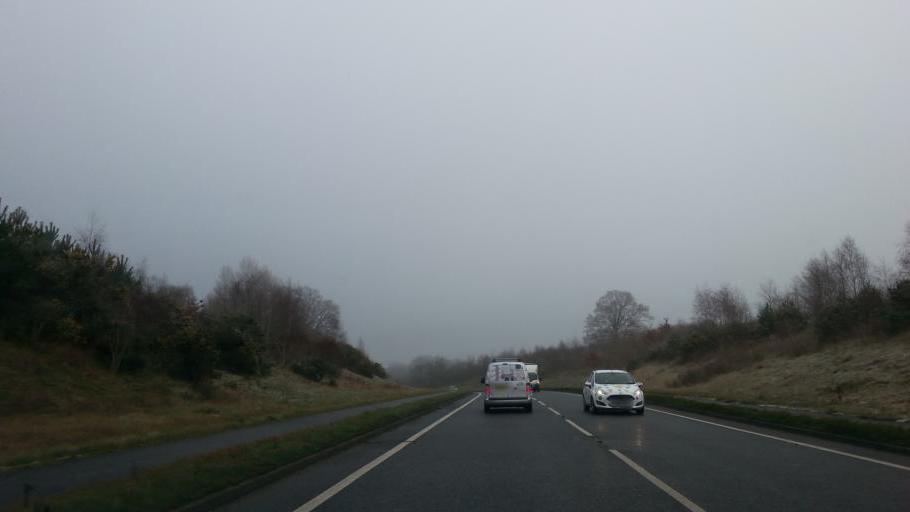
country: GB
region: England
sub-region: Cheshire East
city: Alderley Edge
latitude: 53.3084
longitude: -2.2425
